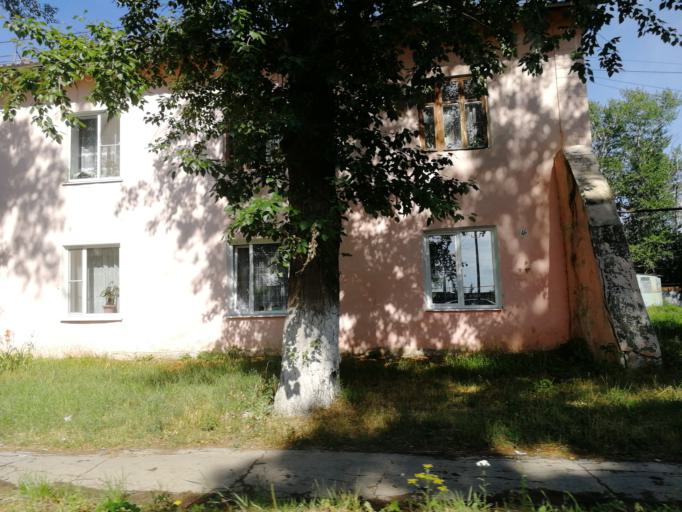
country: RU
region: Tula
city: Bogoroditsk
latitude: 53.7670
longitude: 38.1227
